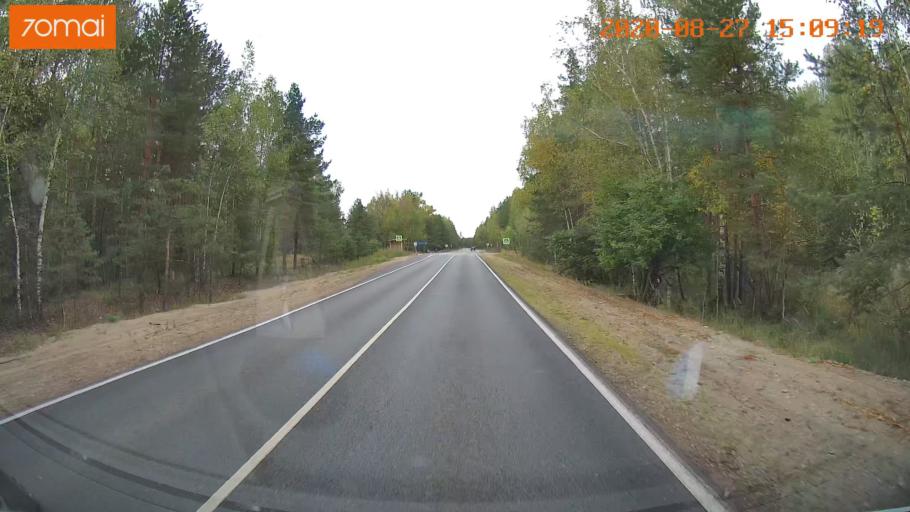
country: RU
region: Vladimir
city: Kurlovo
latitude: 55.5035
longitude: 40.5719
